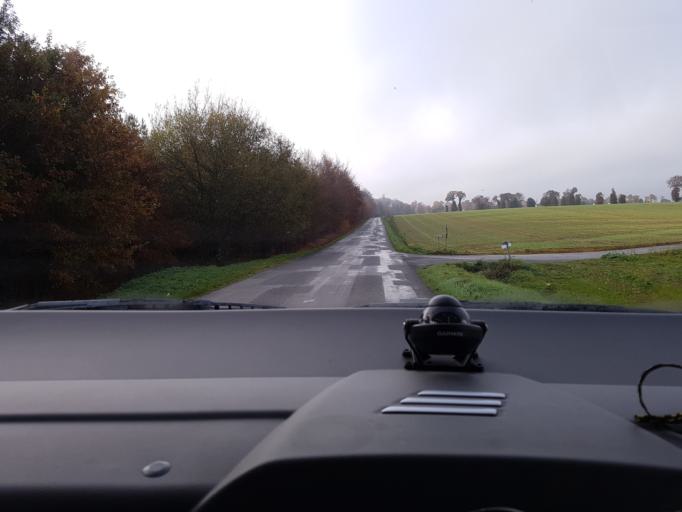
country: FR
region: Brittany
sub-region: Departement d'Ille-et-Vilaine
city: Chevaigne
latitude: 48.1893
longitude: -1.6062
